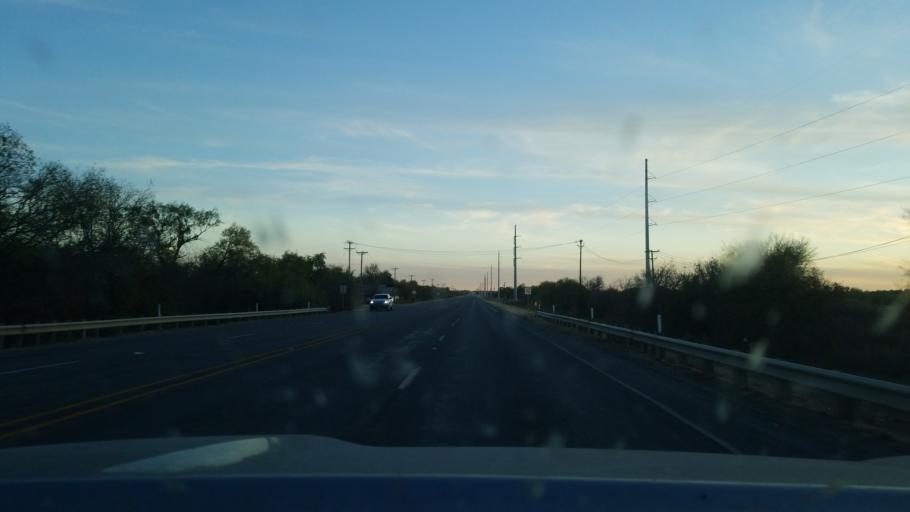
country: US
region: Texas
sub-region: Stephens County
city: Breckenridge
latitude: 32.7406
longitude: -98.9027
